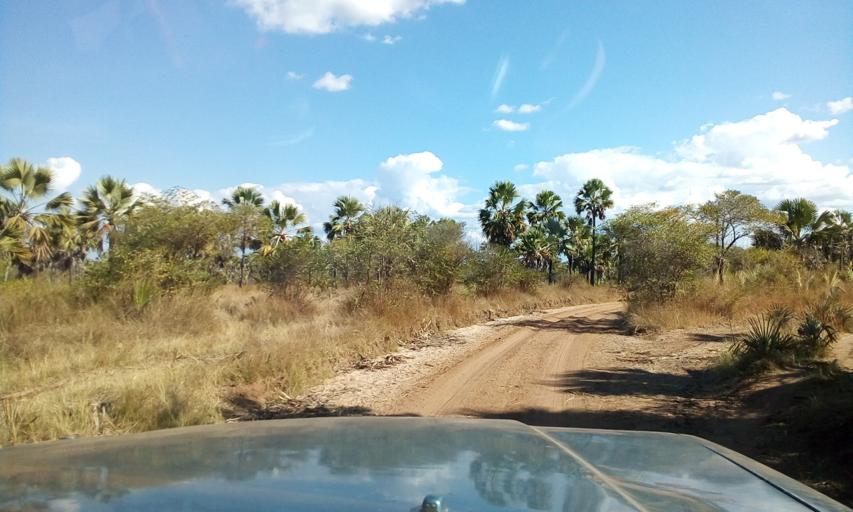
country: MG
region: Boeny
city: Mahajanga
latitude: -16.0615
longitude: 45.7950
